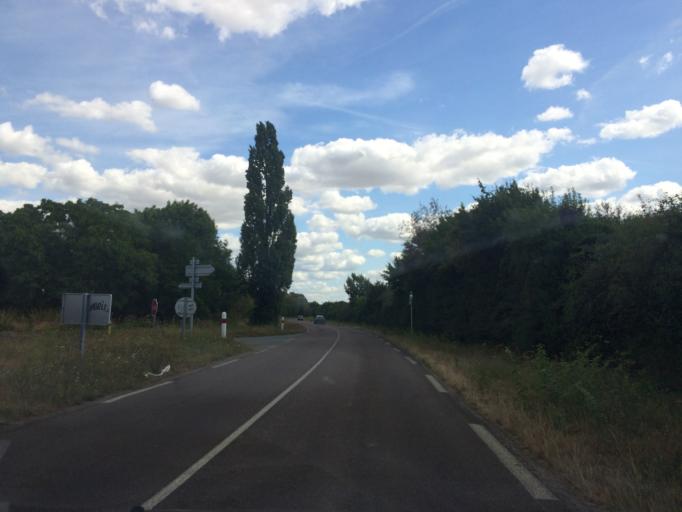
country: FR
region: Ile-de-France
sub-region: Departement de l'Essonne
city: Leudeville
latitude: 48.5508
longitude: 2.3155
